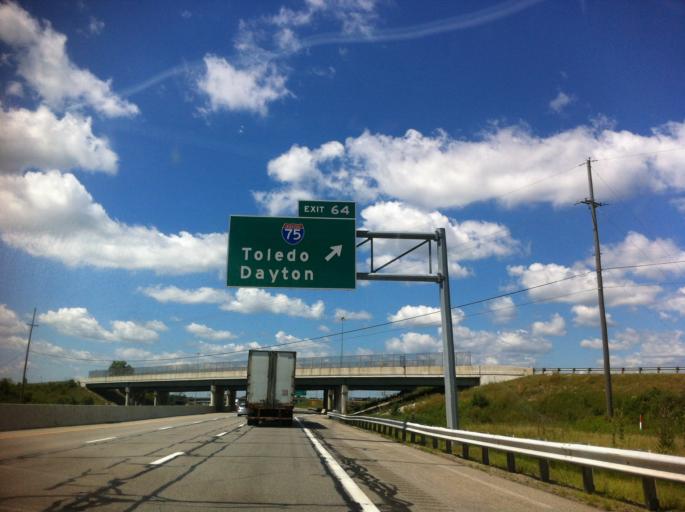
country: US
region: Ohio
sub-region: Wood County
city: Rossford
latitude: 41.5640
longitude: -83.5700
